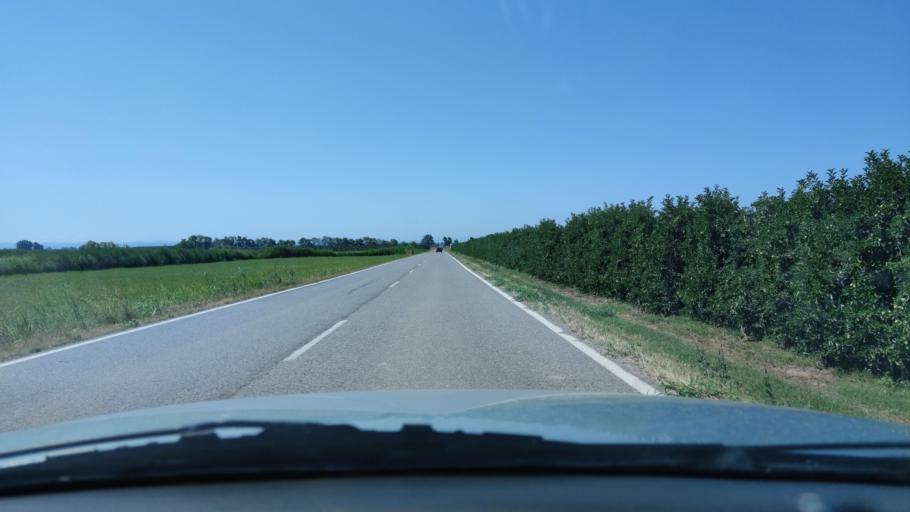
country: ES
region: Catalonia
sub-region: Provincia de Lleida
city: Penelles
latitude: 41.7249
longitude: 0.9826
